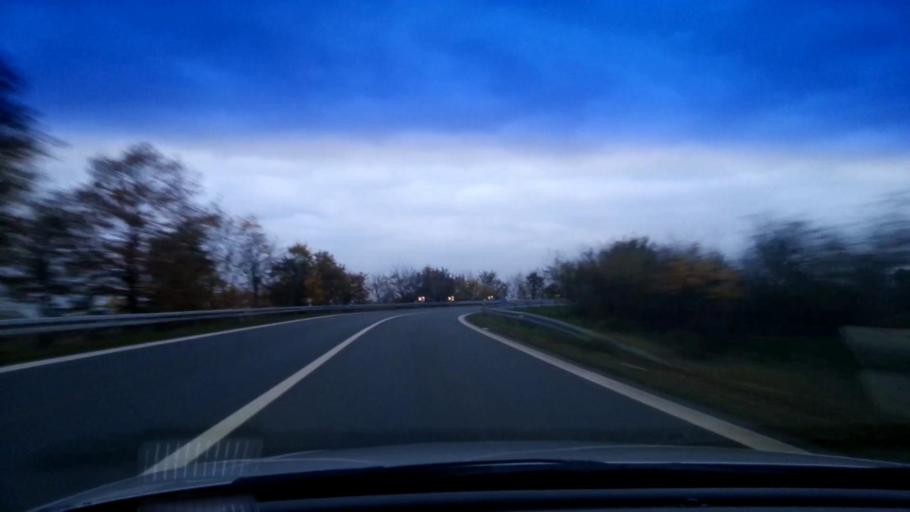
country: DE
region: Bavaria
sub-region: Upper Franconia
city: Kemmern
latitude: 49.9590
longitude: 10.8825
